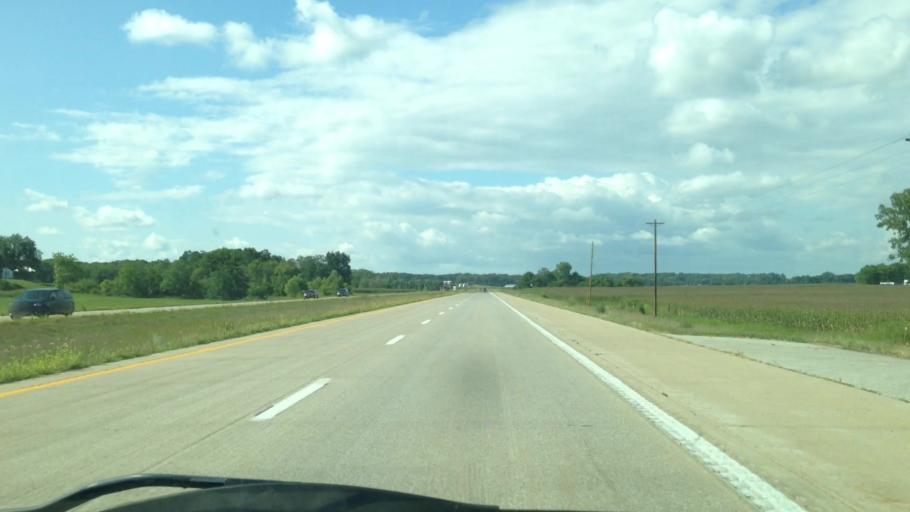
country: US
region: Illinois
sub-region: Hancock County
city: Warsaw
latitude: 40.3200
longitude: -91.5785
